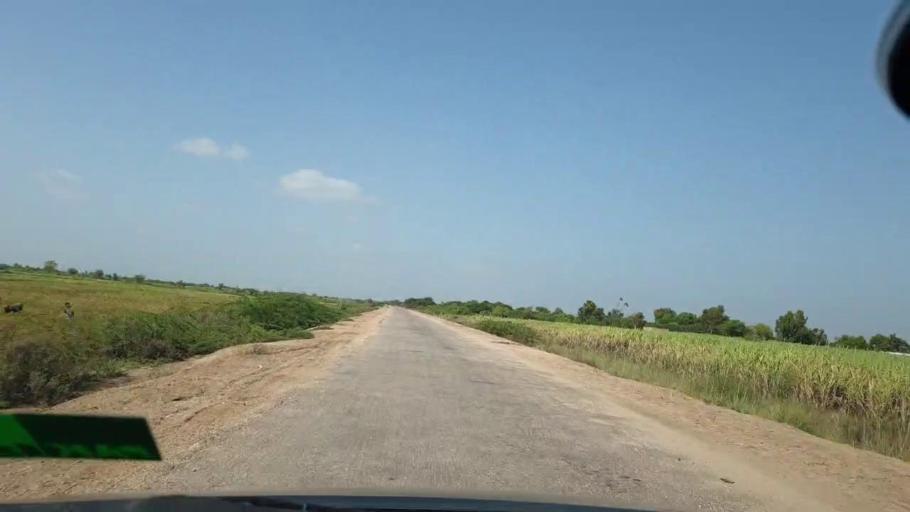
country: PK
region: Sindh
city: Tando Bago
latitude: 24.6883
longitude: 69.1883
